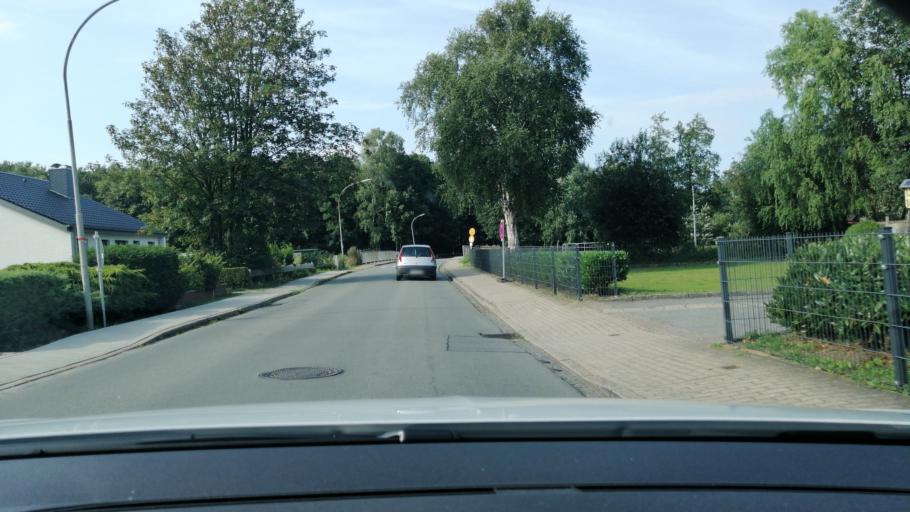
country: DE
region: Schleswig-Holstein
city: Leck
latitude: 54.7725
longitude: 8.9614
